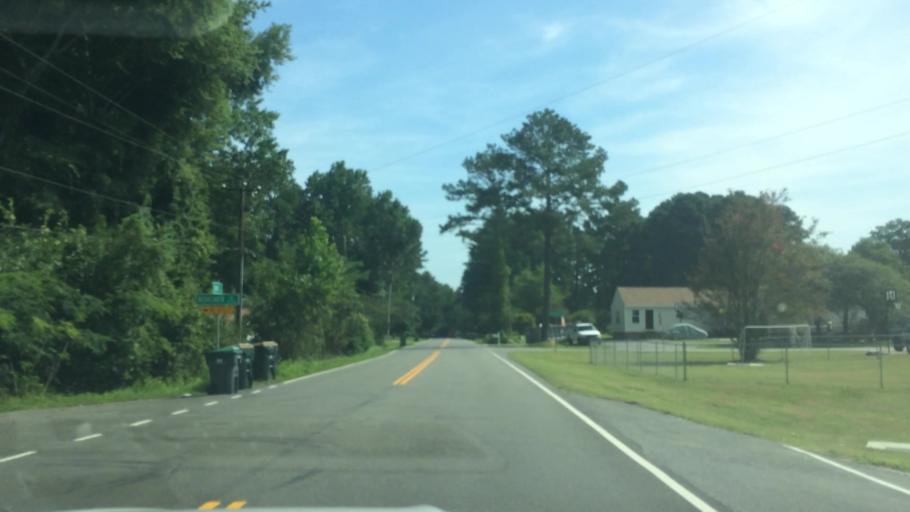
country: US
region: Virginia
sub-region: York County
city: Yorktown
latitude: 37.1647
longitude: -76.4534
